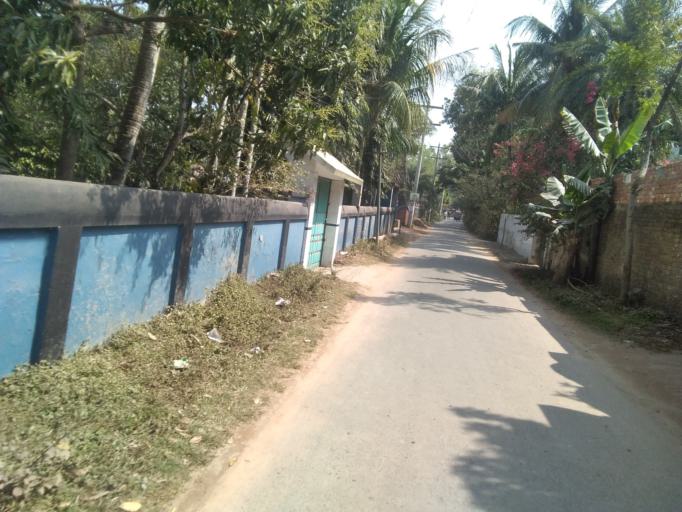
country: IN
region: West Bengal
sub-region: North 24 Parganas
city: Taki
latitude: 22.5905
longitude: 88.9968
